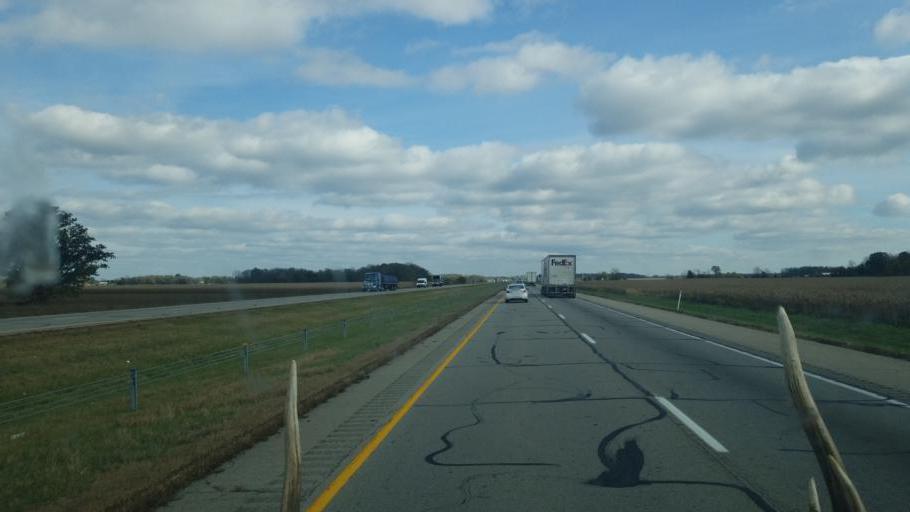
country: US
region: Indiana
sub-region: Henry County
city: New Castle
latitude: 39.8523
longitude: -85.2936
